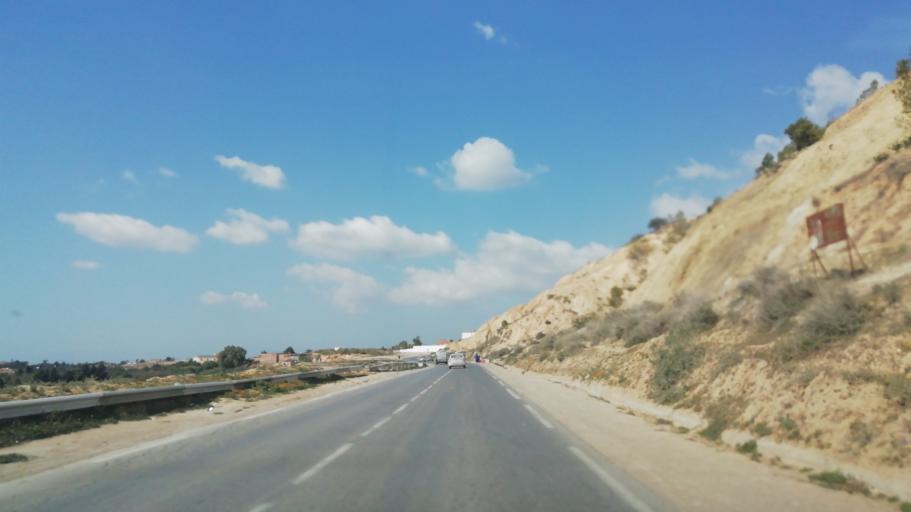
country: DZ
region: Mascara
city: Mascara
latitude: 35.5682
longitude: 0.0709
